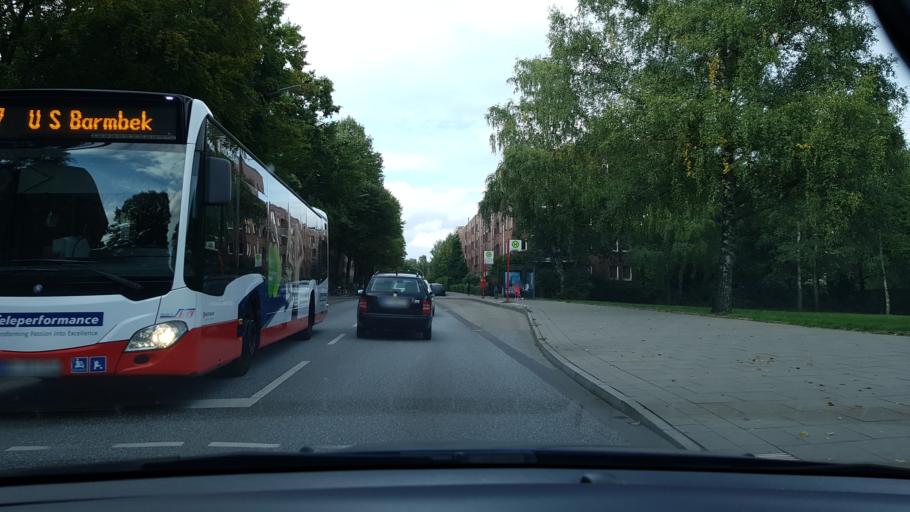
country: DE
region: Hamburg
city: Barmbek-Nord
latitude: 53.5994
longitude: 10.0508
